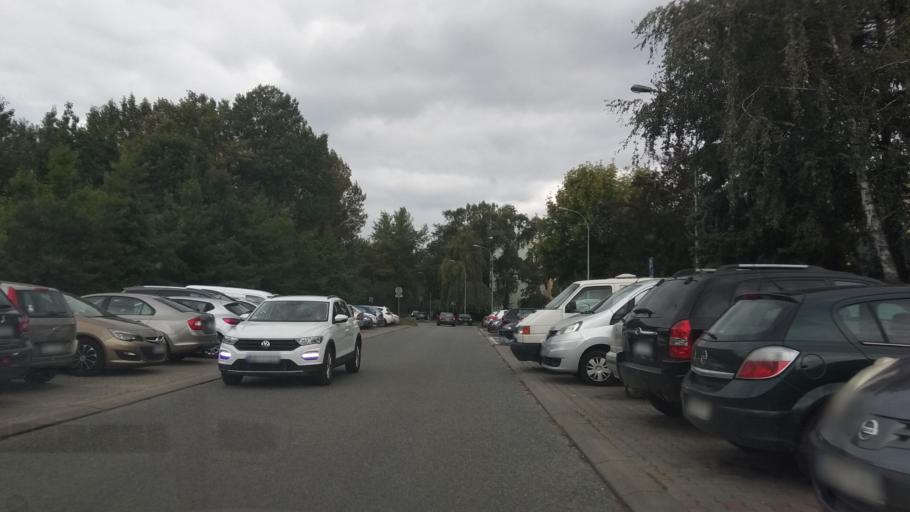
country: PL
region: Masovian Voivodeship
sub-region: Warszawa
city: Bemowo
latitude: 52.2352
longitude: 20.9092
